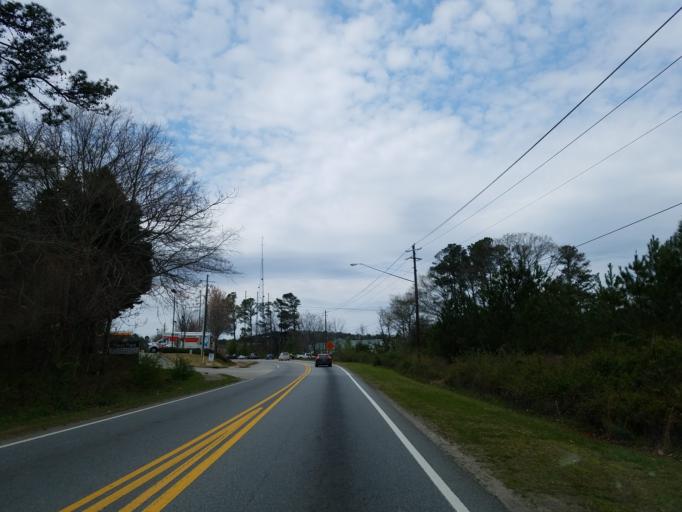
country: US
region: Georgia
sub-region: Fulton County
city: Alpharetta
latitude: 34.0597
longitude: -84.3003
